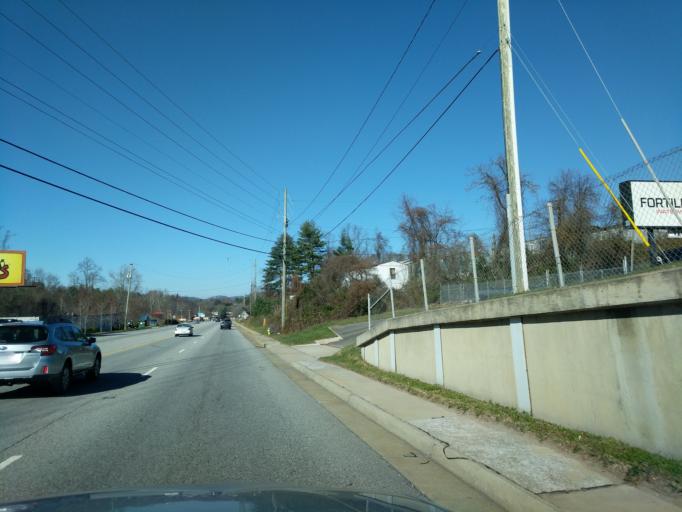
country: US
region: North Carolina
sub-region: Buncombe County
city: Biltmore Forest
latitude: 35.5376
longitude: -82.5199
